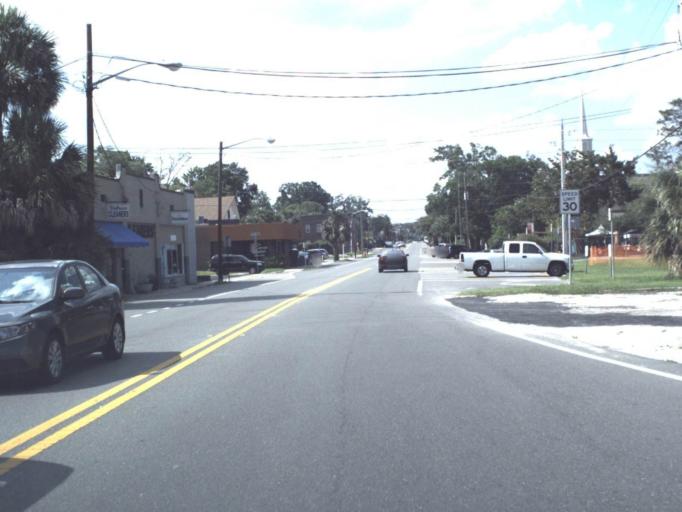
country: US
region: Florida
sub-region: Duval County
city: Jacksonville
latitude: 30.2824
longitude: -81.7135
